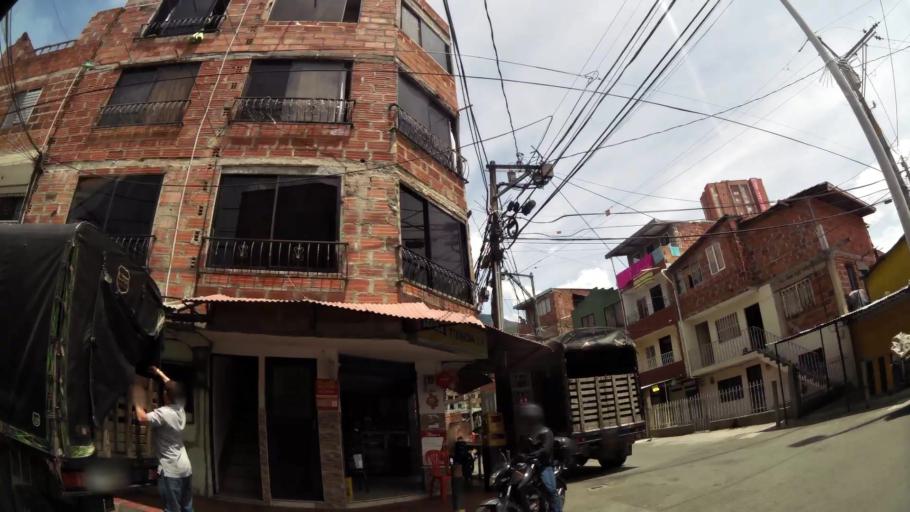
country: CO
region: Antioquia
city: Bello
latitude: 6.3374
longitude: -75.5533
